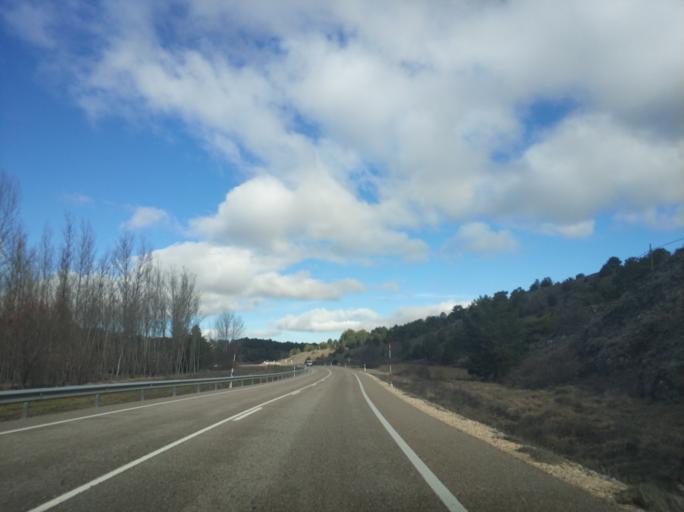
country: ES
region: Castille and Leon
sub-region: Provincia de Burgos
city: Rabanera del Pinar
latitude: 41.8699
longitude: -3.2151
